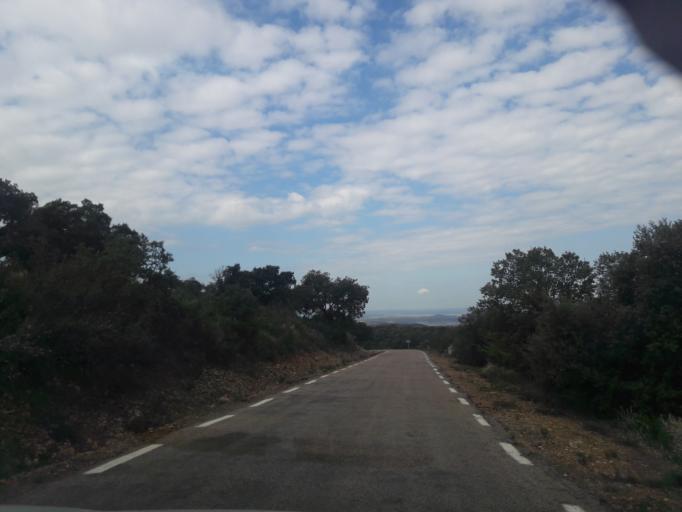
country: ES
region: Castille and Leon
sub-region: Provincia de Salamanca
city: Serradilla del Arroyo
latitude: 40.5405
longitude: -6.3926
